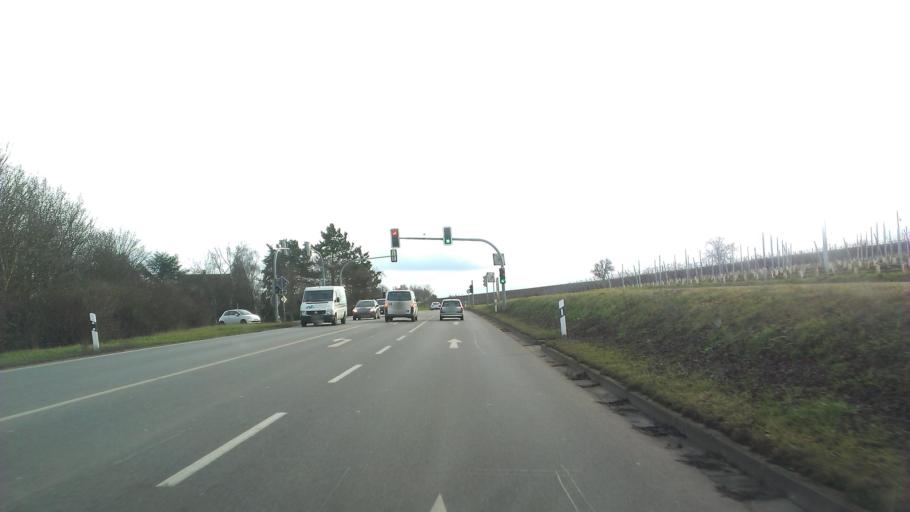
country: DE
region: Rheinland-Pfalz
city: Bretzenheim
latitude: 49.8485
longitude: 7.9072
